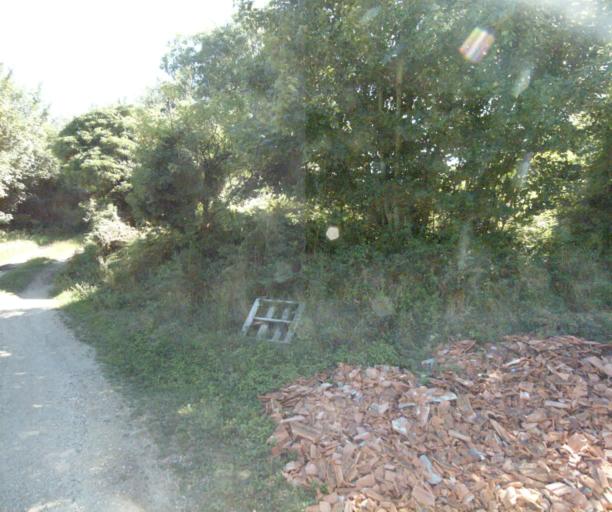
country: FR
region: Midi-Pyrenees
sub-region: Departement du Tarn
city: Dourgne
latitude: 43.4360
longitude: 2.1374
